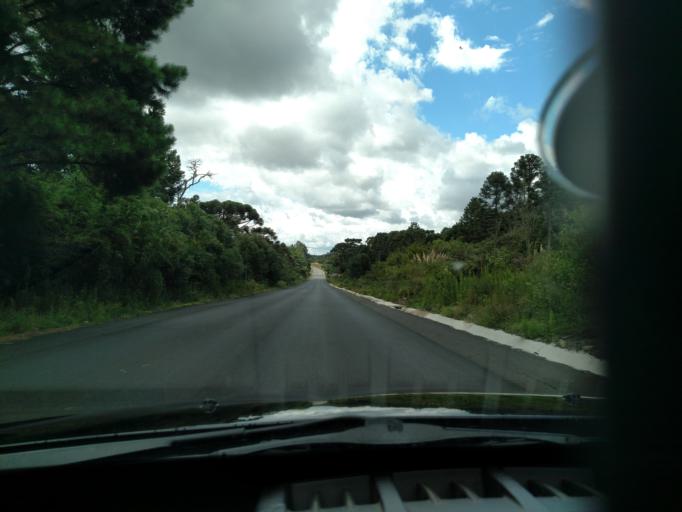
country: BR
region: Santa Catarina
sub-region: Lages
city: Lages
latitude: -27.9565
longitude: -50.0963
